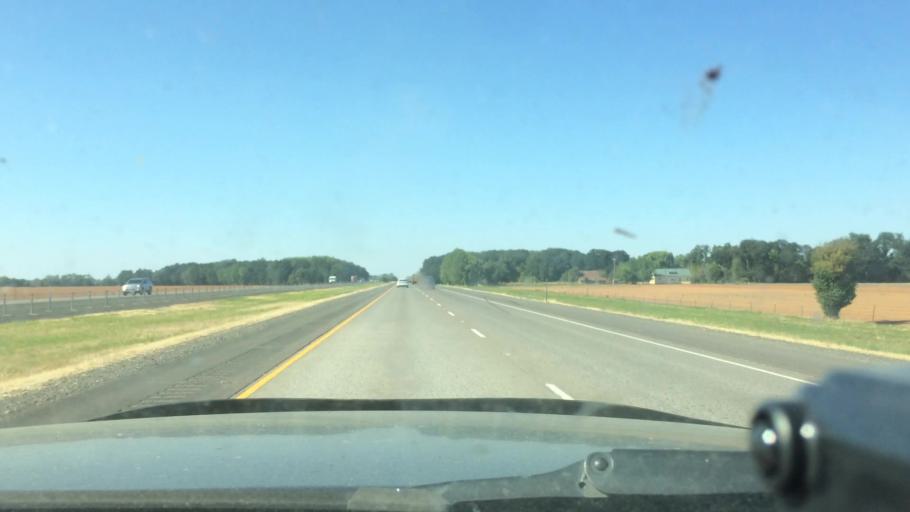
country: US
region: Oregon
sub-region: Linn County
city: Tangent
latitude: 44.4665
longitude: -123.0610
